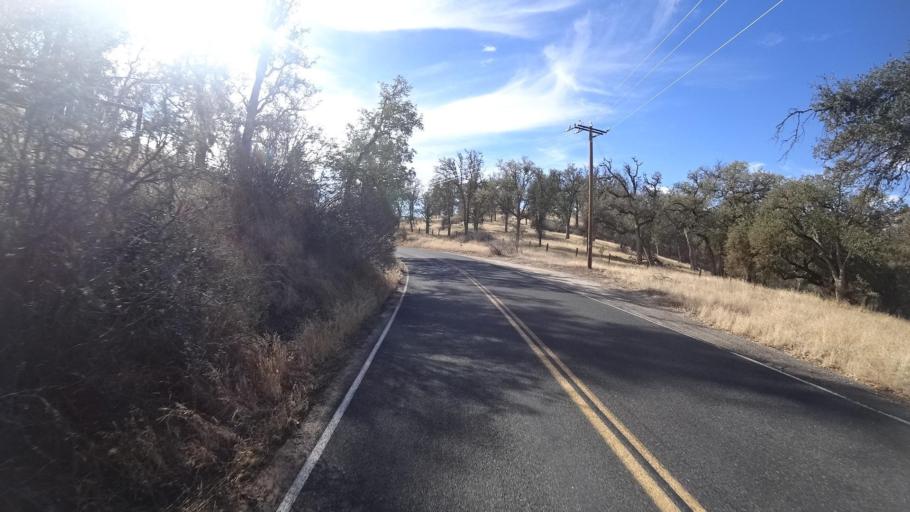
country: US
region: California
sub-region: Kern County
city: Alta Sierra
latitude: 35.6878
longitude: -118.7315
